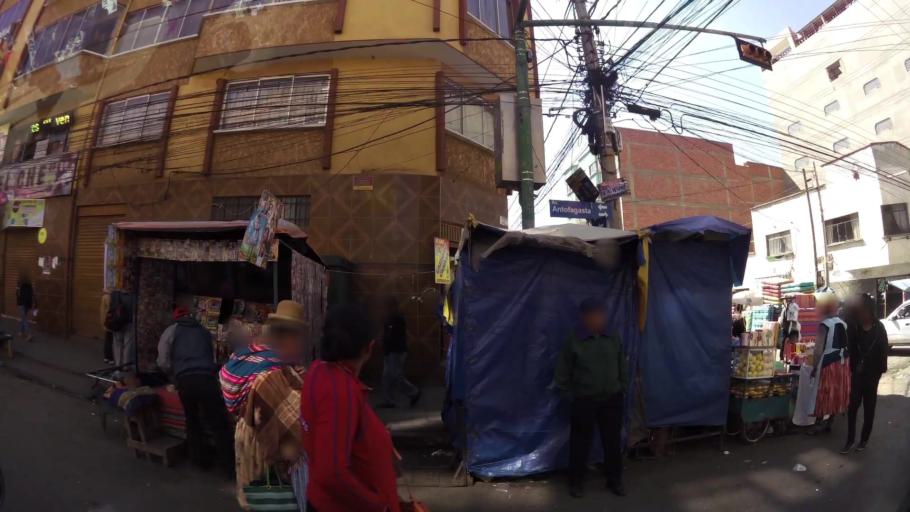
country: BO
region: La Paz
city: La Paz
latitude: -16.5073
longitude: -68.1598
